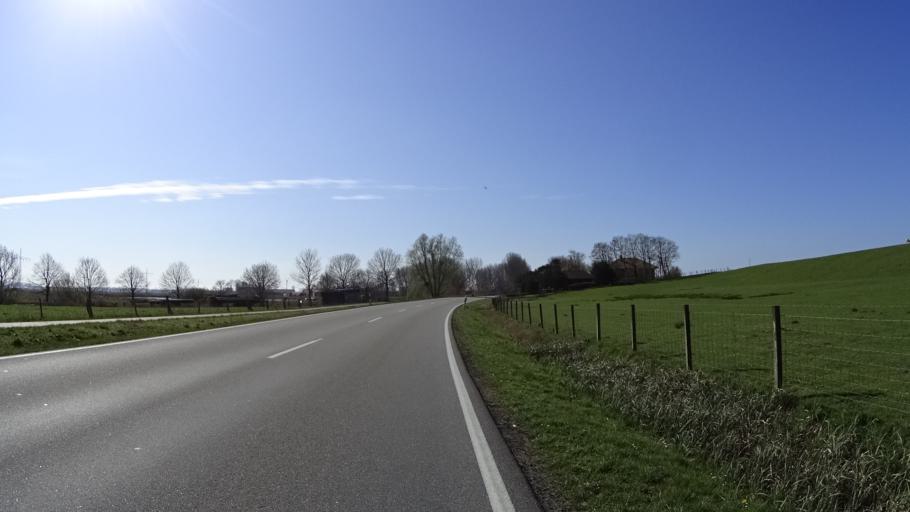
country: DE
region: Lower Saxony
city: Jemgum
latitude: 53.2871
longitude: 7.4048
